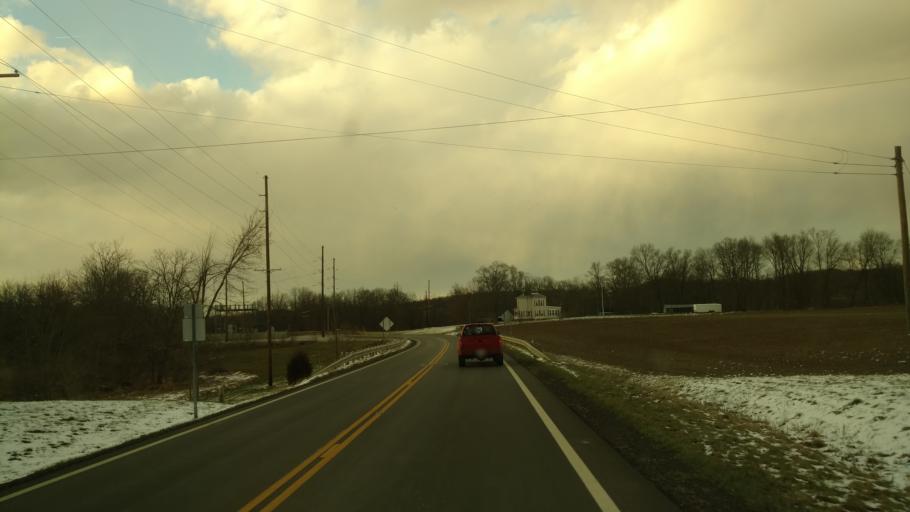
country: US
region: Ohio
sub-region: Ashland County
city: Ashland
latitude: 40.7868
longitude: -82.1849
